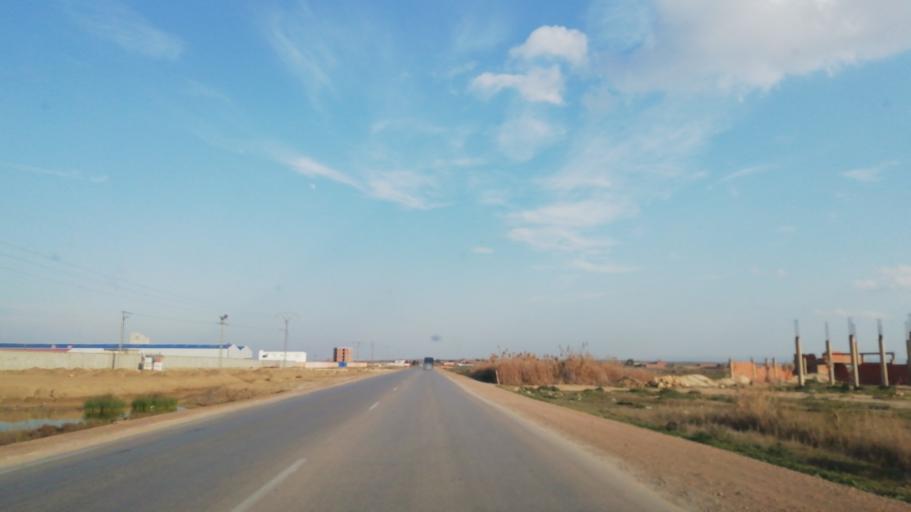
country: DZ
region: Relizane
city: Relizane
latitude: 35.8979
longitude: 0.5759
